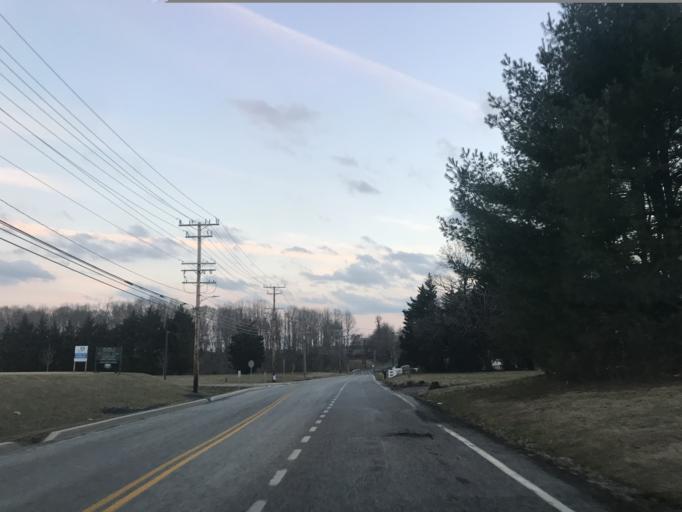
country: US
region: Maryland
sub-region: Harford County
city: South Bel Air
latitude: 39.5505
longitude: -76.2867
